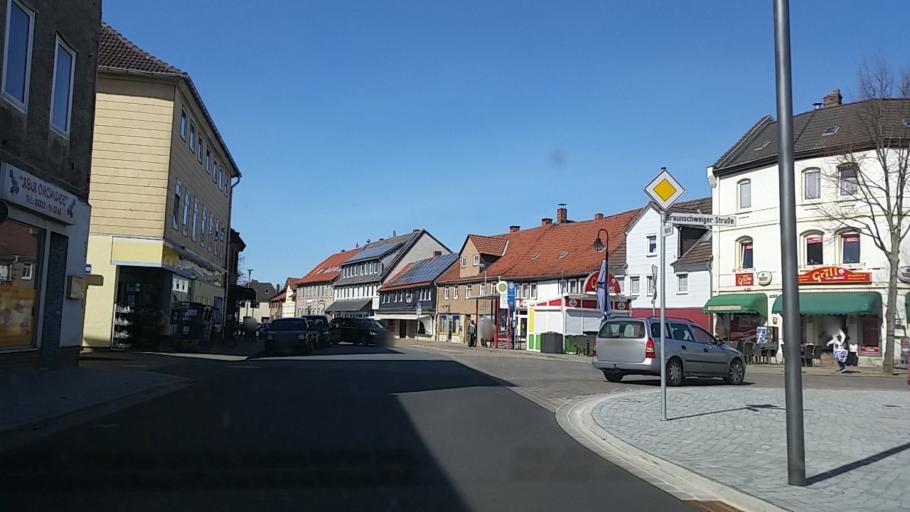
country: DE
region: Lower Saxony
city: Schoppenstedt
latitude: 52.1443
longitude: 10.7750
